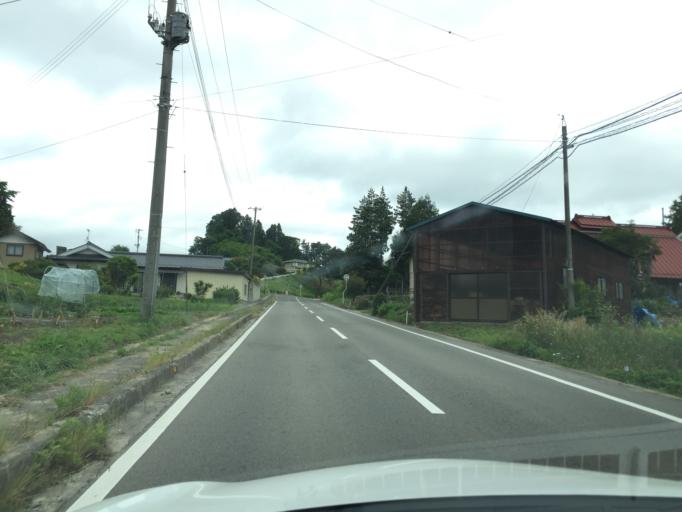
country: JP
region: Fukushima
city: Funehikimachi-funehiki
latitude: 37.4217
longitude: 140.5496
